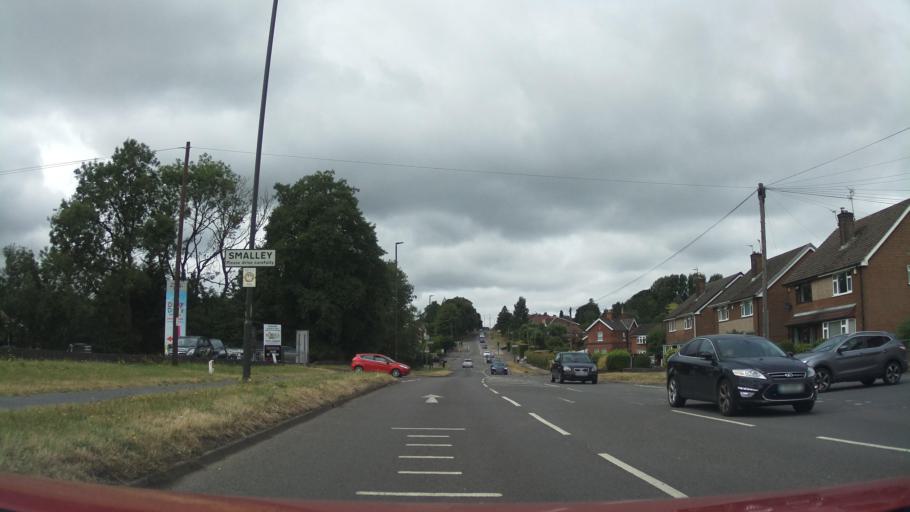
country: GB
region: England
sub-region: Derbyshire
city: Heanor
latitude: 53.0109
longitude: -1.3668
